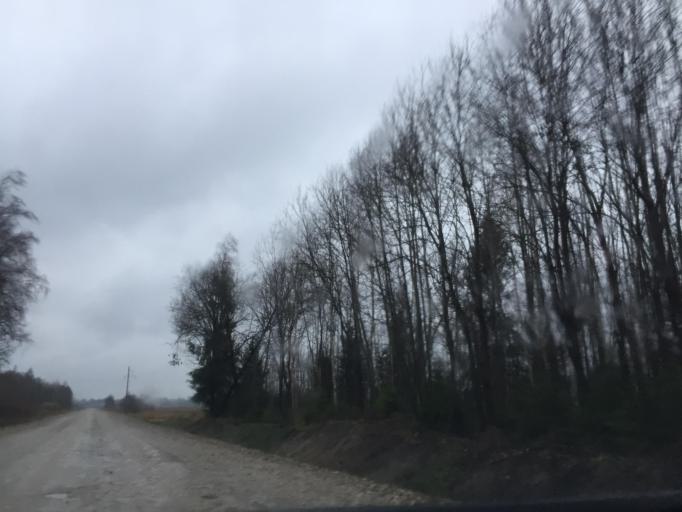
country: LV
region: Salacgrivas
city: Salacgriva
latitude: 57.7628
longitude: 24.5515
